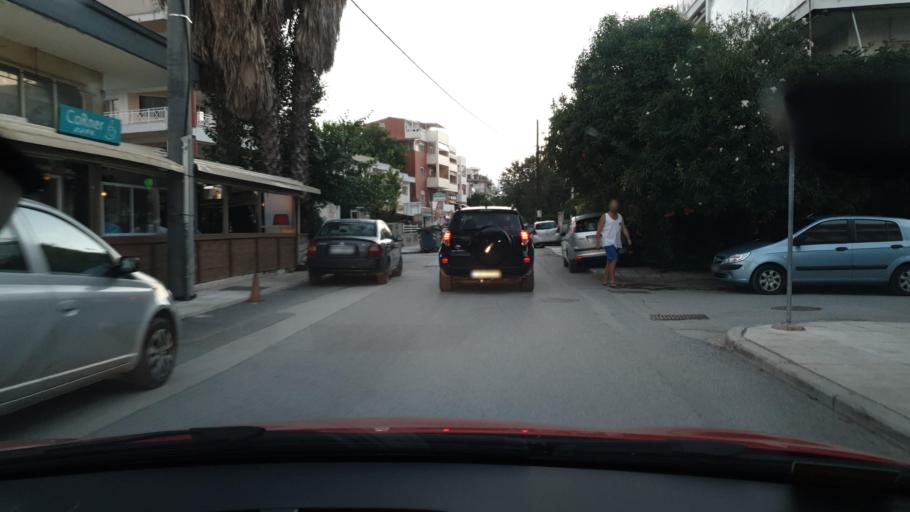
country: GR
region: Central Macedonia
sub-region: Nomos Thessalonikis
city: Peraia
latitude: 40.5090
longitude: 22.9280
